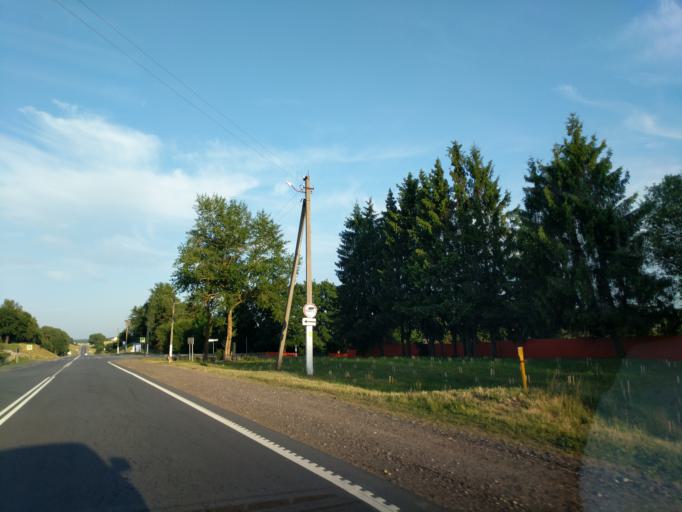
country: BY
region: Minsk
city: Syomkava
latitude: 54.1083
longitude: 27.4606
